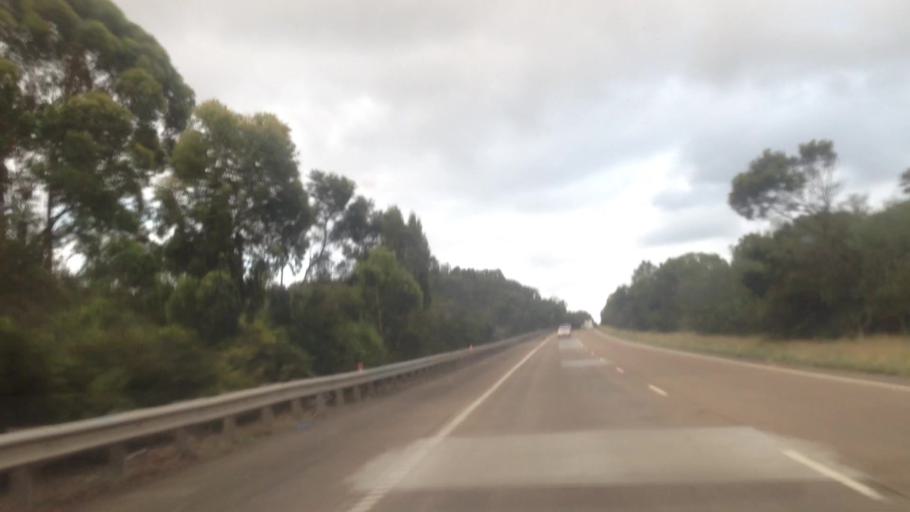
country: AU
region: New South Wales
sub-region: Wyong Shire
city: Charmhaven
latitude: -33.1556
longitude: 151.4708
